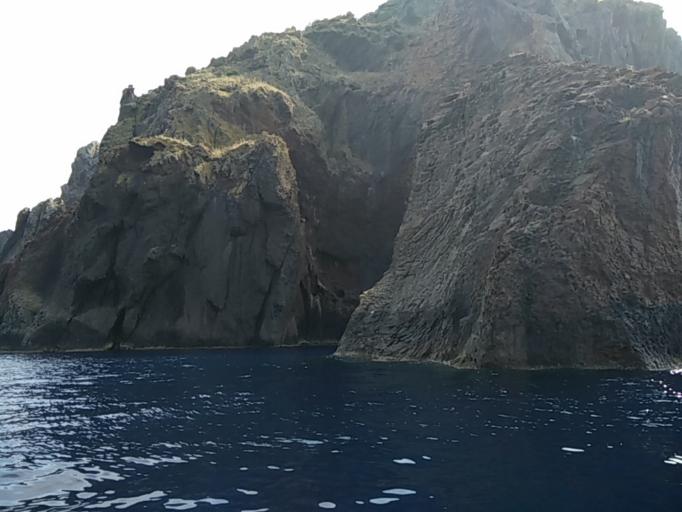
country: FR
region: Corsica
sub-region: Departement de la Corse-du-Sud
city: Cargese
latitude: 42.3802
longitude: 8.5506
